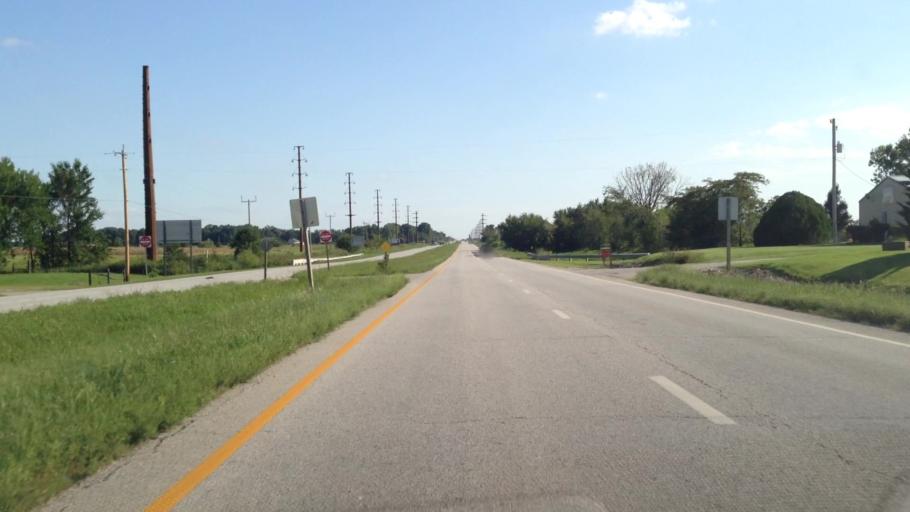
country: US
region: Kansas
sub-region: Crawford County
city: Arma
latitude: 37.5071
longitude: -94.7053
